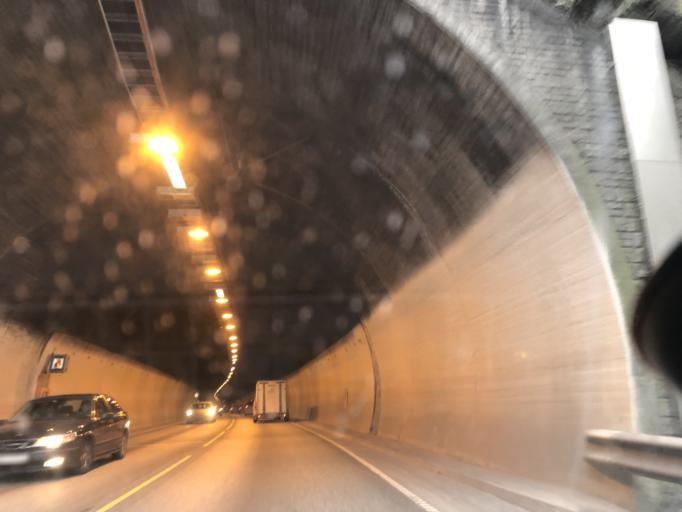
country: NO
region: Rogaland
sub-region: Stavanger
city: Stavanger
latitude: 58.9753
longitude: 5.6928
